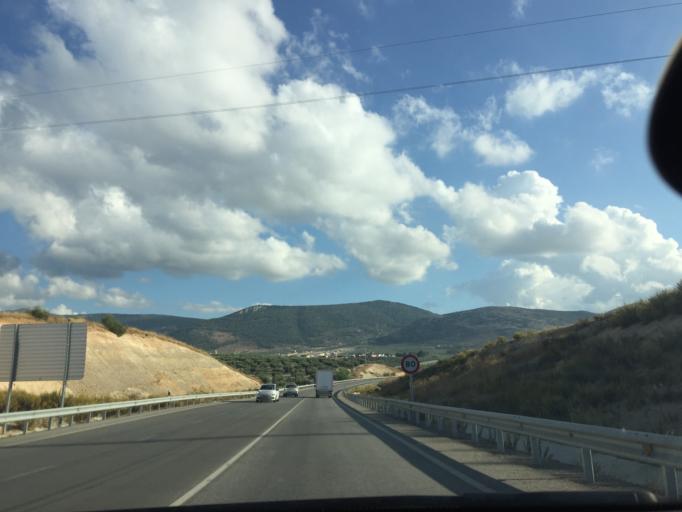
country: ES
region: Andalusia
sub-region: Provincia de Jaen
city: Mancha Real
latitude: 37.8036
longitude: -3.6258
